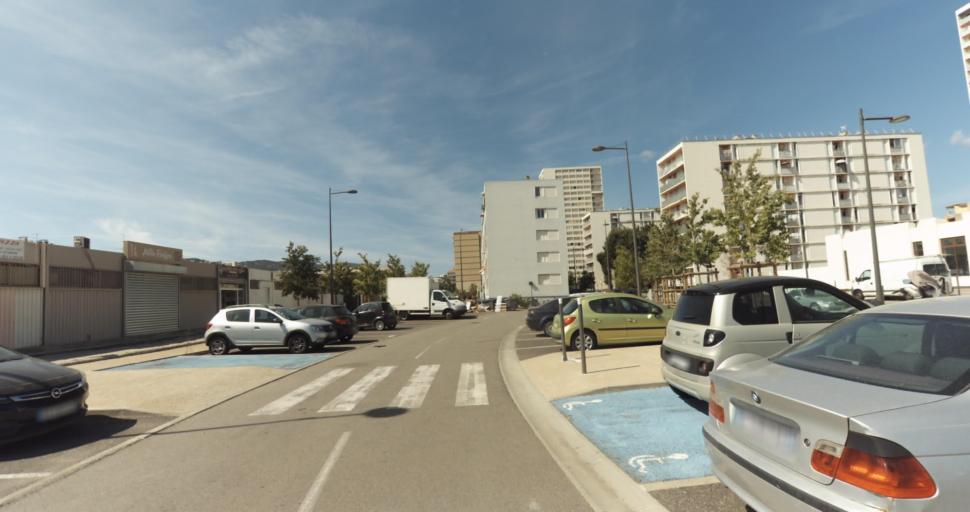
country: FR
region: Corsica
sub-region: Departement de la Corse-du-Sud
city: Ajaccio
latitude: 41.9349
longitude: 8.7501
